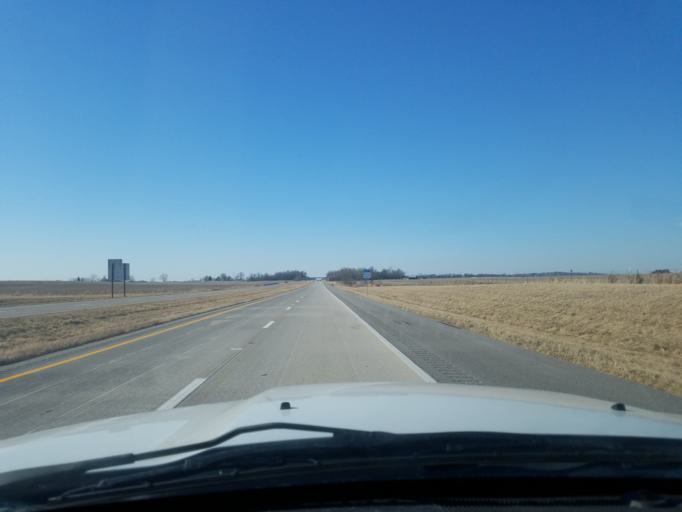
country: US
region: Kentucky
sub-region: Henderson County
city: Henderson
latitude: 37.7893
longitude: -87.4810
